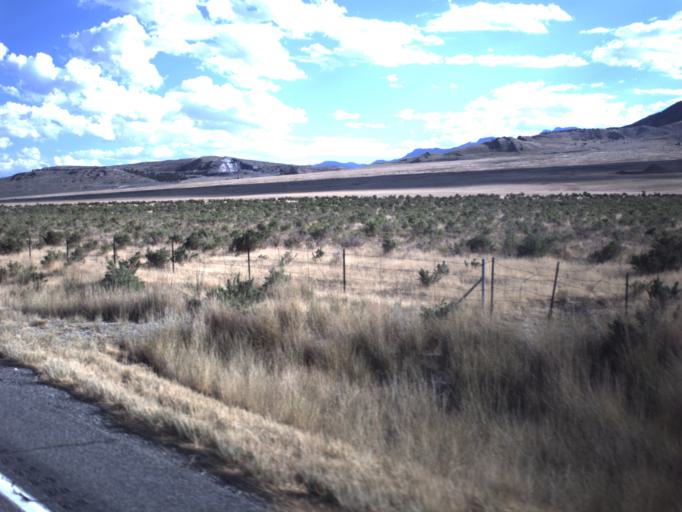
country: US
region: Utah
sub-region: Tooele County
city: Grantsville
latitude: 40.6653
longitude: -112.5428
